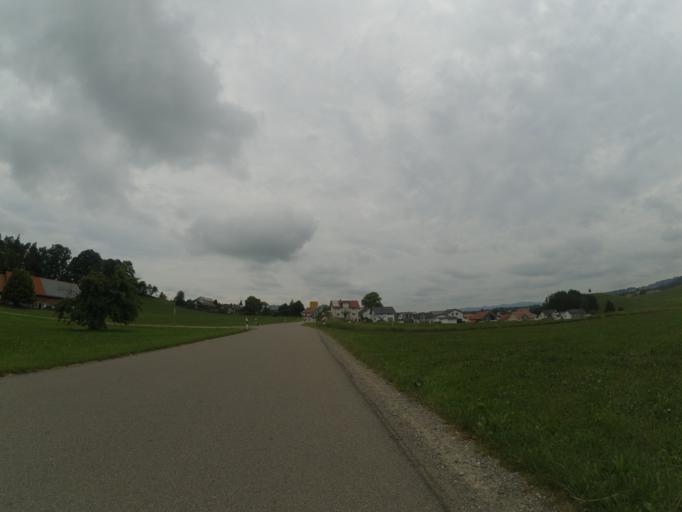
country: DE
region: Bavaria
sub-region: Swabia
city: Gestratz
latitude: 47.6852
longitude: 9.9523
